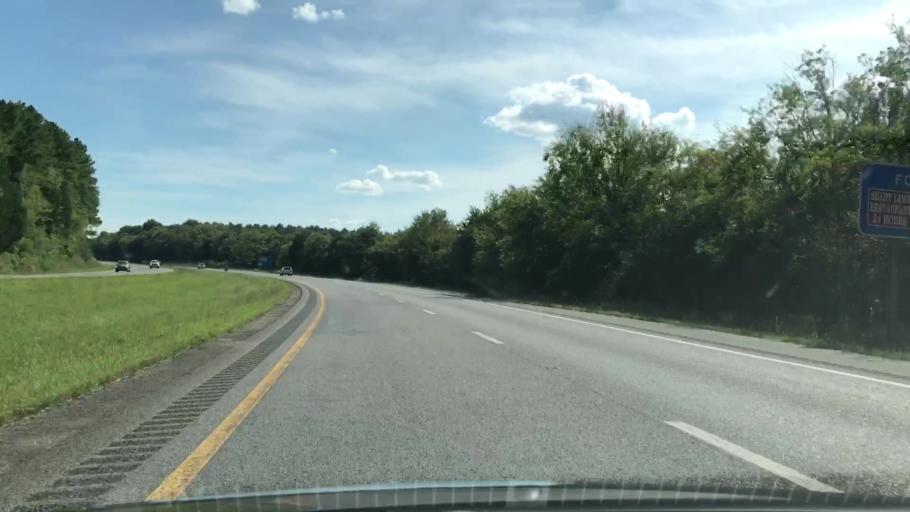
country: US
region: Alabama
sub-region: Limestone County
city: Ardmore
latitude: 35.1066
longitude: -86.8854
